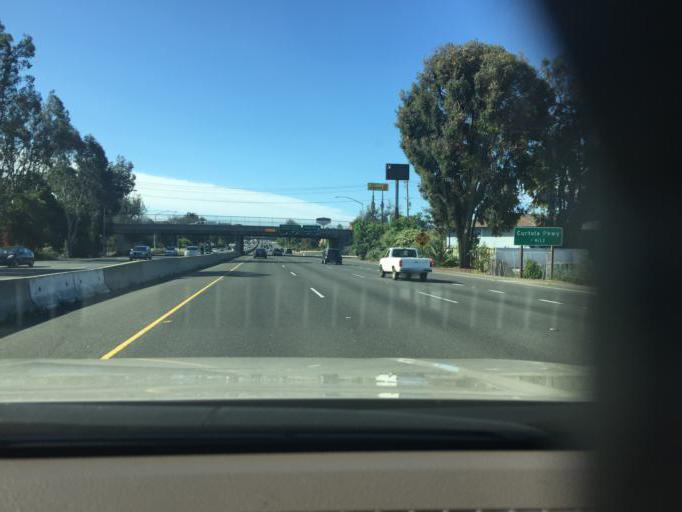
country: US
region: California
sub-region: Solano County
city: Vallejo
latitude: 38.1069
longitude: -122.2298
